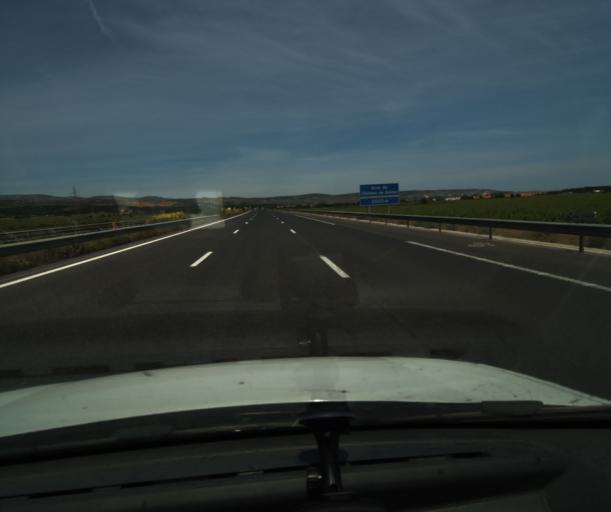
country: FR
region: Languedoc-Roussillon
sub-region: Departement des Pyrenees-Orientales
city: Salses-le-Chateau
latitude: 42.8186
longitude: 2.9084
